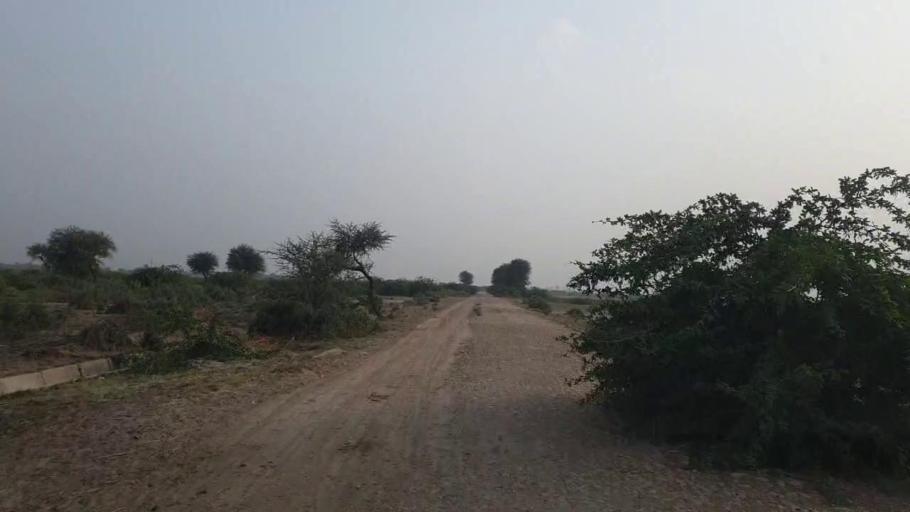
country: PK
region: Sindh
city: Mirpur Batoro
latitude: 24.6486
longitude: 68.3727
